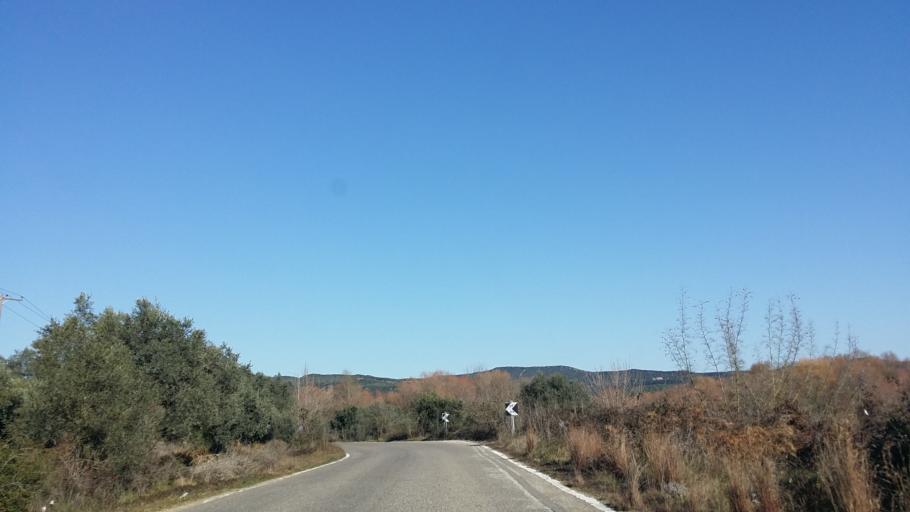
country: GR
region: West Greece
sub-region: Nomos Aitolias kai Akarnanias
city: Lepenou
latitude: 38.7277
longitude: 21.3342
